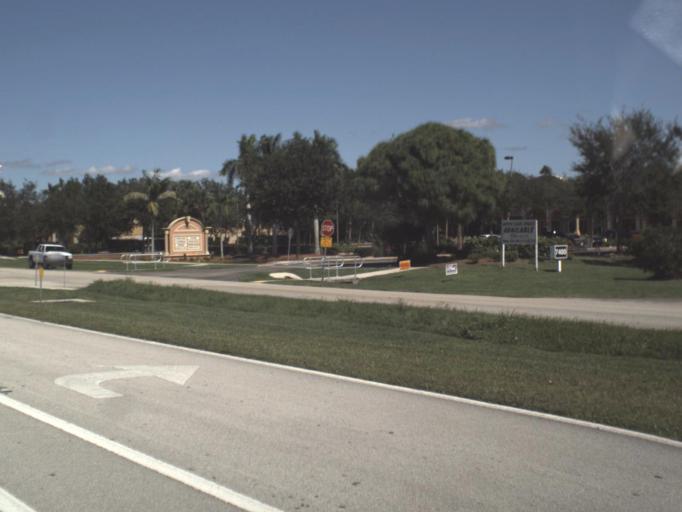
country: US
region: Florida
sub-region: Collier County
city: Pelican Bay
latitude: 26.2446
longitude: -81.8009
